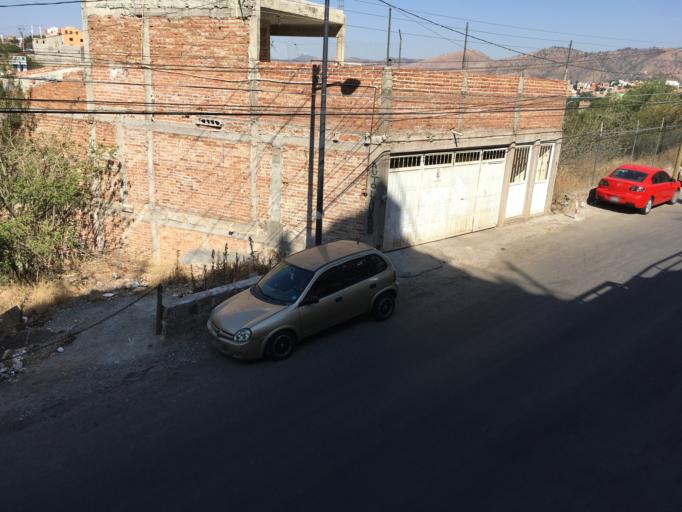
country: MX
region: Guanajuato
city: Guanajuato
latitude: 21.0169
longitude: -101.2457
